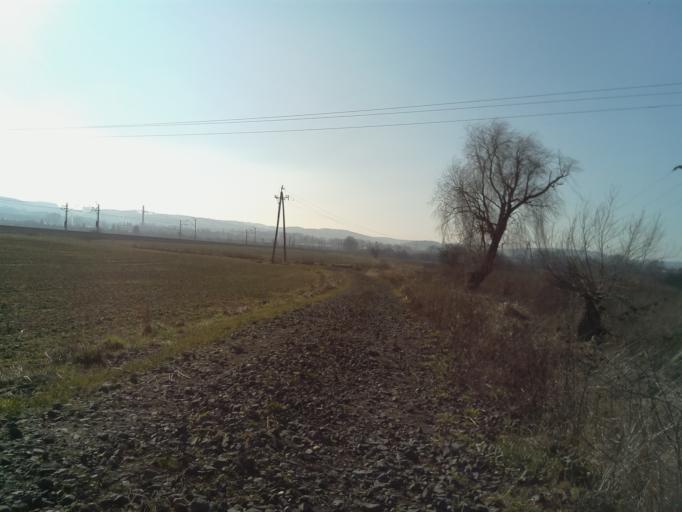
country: PL
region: Lower Silesian Voivodeship
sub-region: Powiat swidnicki
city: Swiebodzice
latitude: 50.8691
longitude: 16.3437
